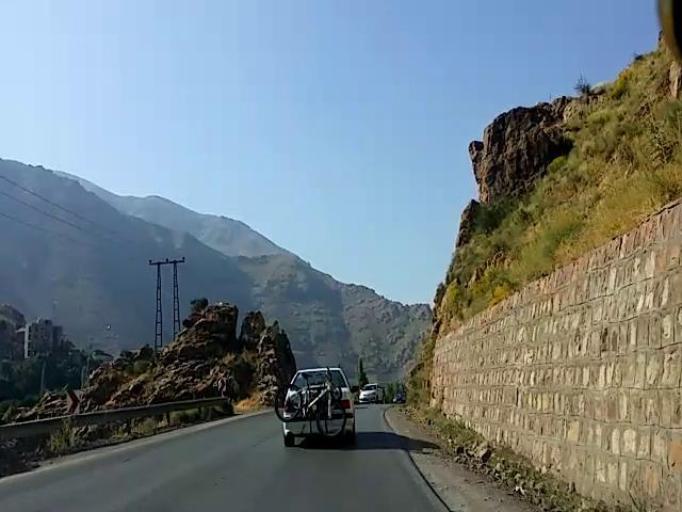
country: IR
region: Tehran
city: Tajrish
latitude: 36.0631
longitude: 51.3095
